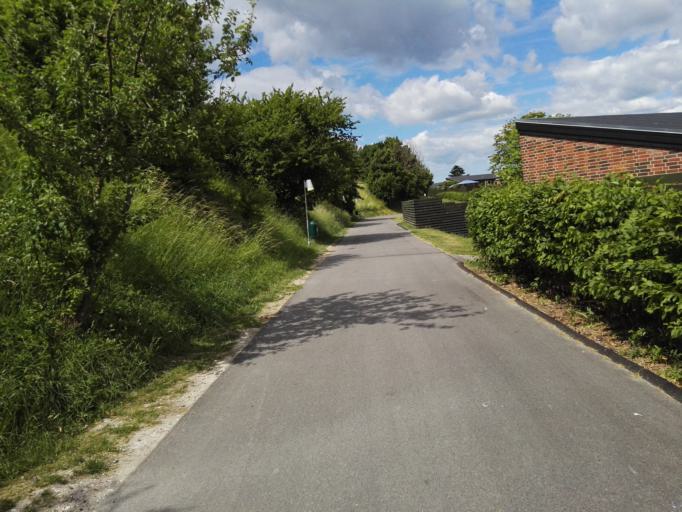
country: DK
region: Capital Region
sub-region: Egedal Kommune
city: Stenlose
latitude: 55.7699
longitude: 12.1893
